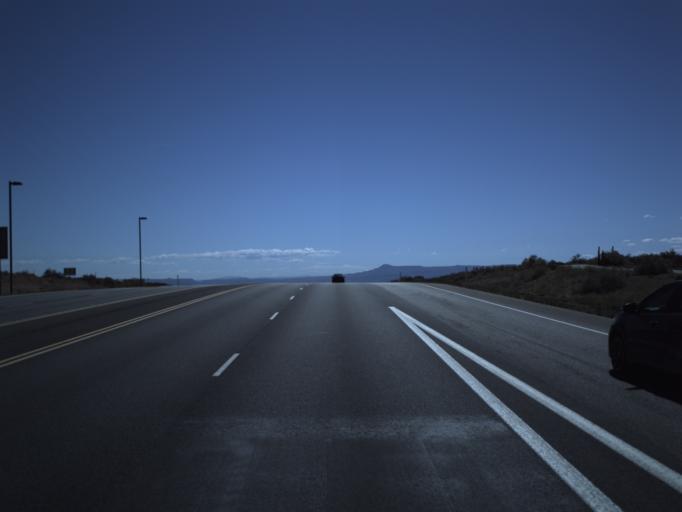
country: US
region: Utah
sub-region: Washington County
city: Ivins
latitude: 37.1911
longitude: -113.6211
